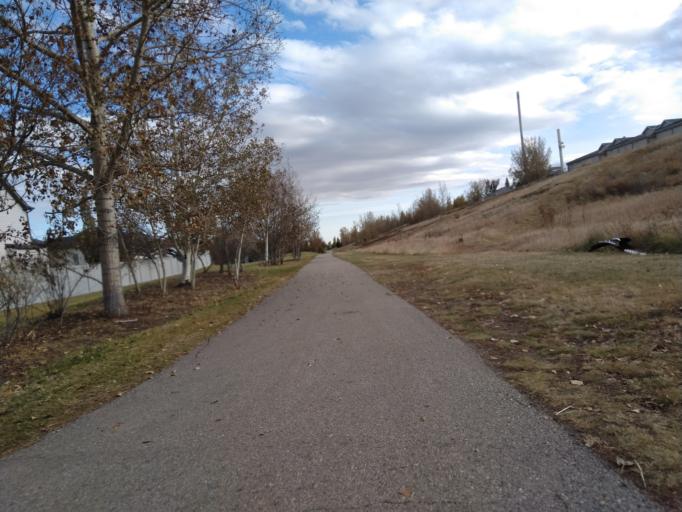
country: CA
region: Alberta
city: Calgary
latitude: 51.1484
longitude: -114.1073
